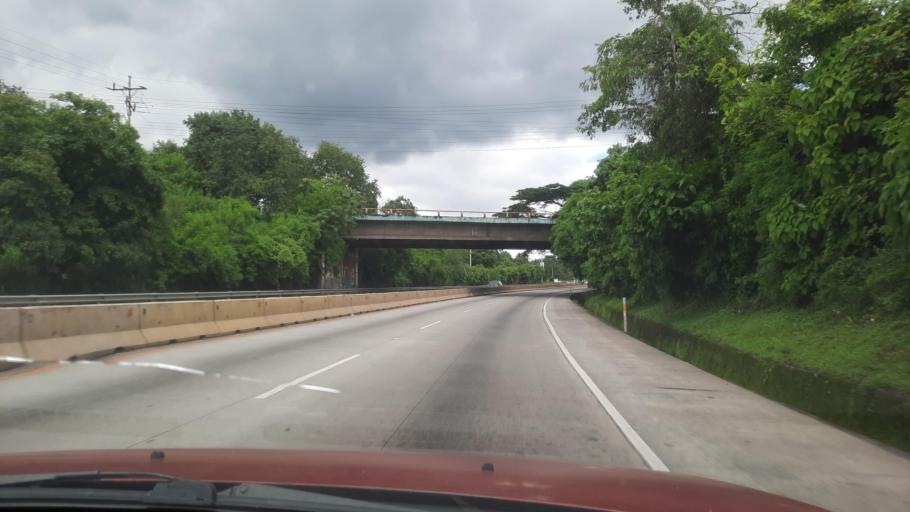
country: SV
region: Sonsonate
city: Sonzacate
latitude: 13.7388
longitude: -89.6959
